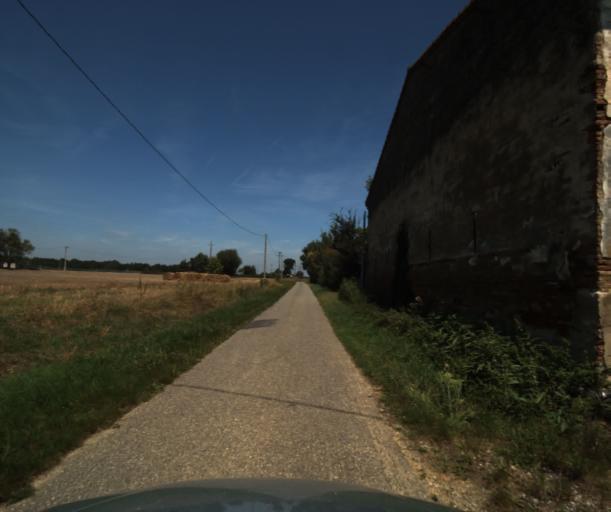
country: FR
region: Midi-Pyrenees
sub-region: Departement de la Haute-Garonne
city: Labastidette
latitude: 43.4606
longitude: 1.2676
